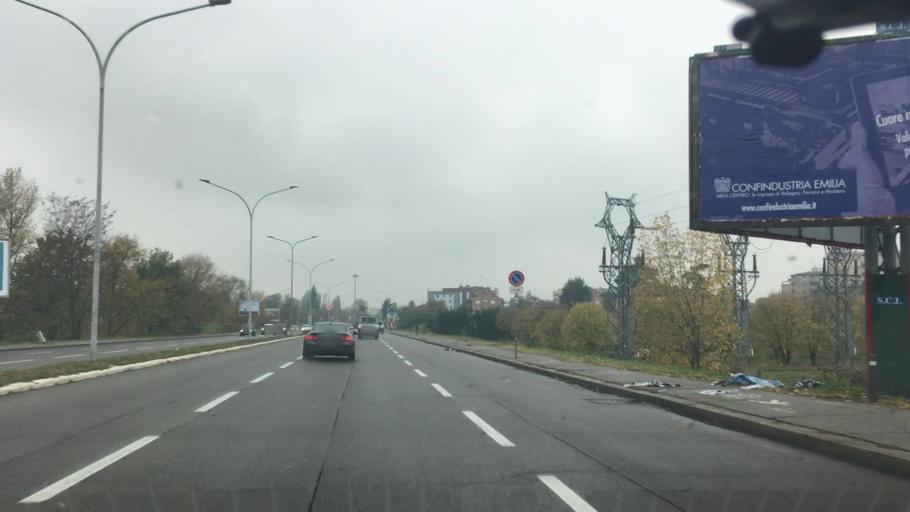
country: IT
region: Emilia-Romagna
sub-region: Provincia di Bologna
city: Casalecchio di Reno
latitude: 44.5061
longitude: 11.2872
